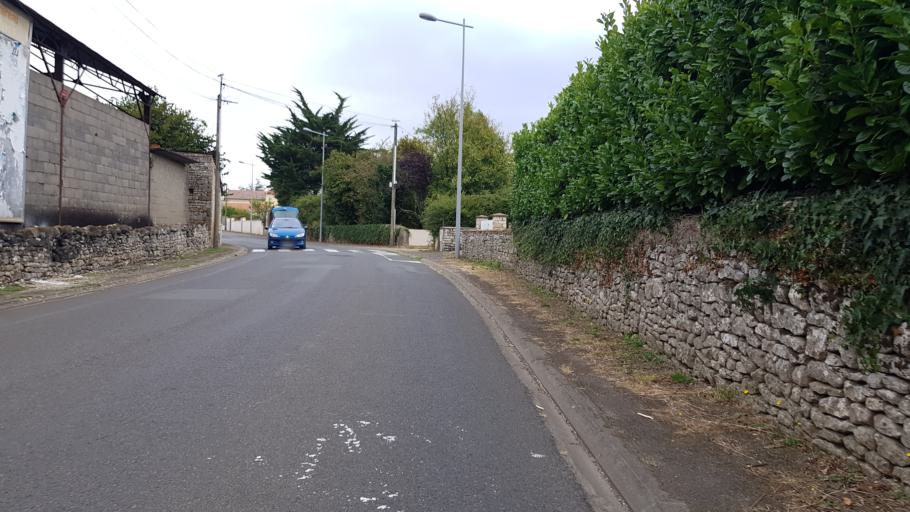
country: FR
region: Poitou-Charentes
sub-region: Departement des Deux-Sevres
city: Vouille
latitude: 46.3161
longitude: -0.3667
